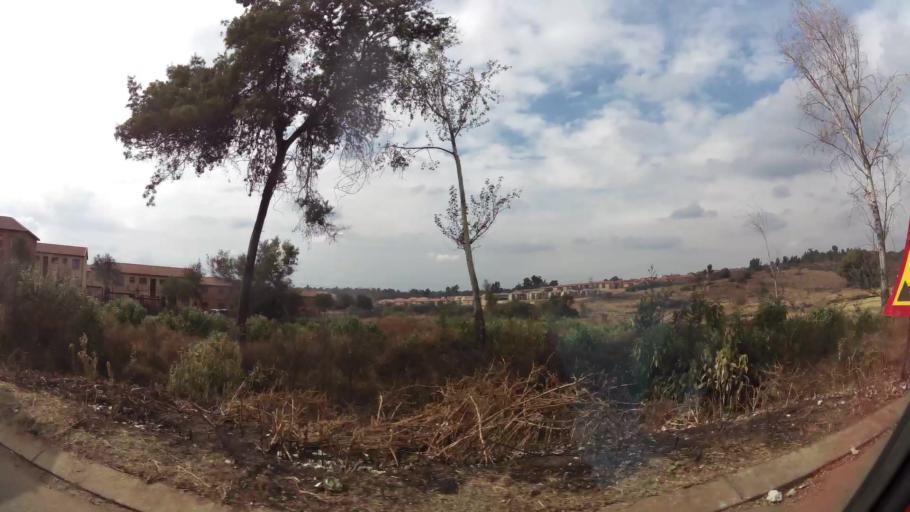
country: ZA
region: Gauteng
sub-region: City of Johannesburg Metropolitan Municipality
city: Roodepoort
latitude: -26.1028
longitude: 27.8872
